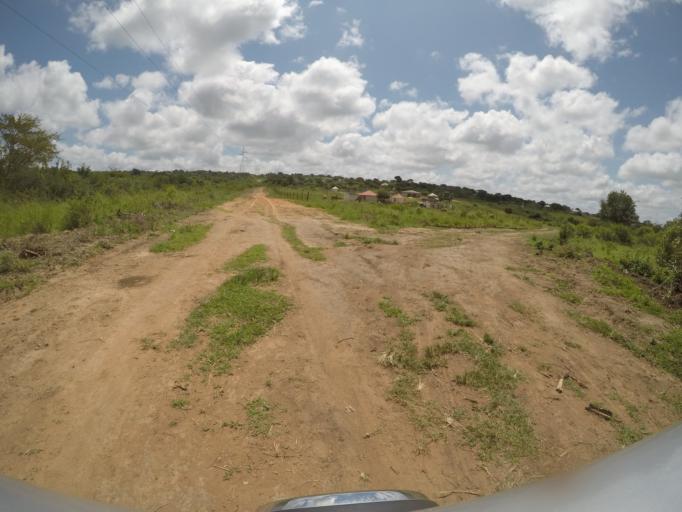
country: ZA
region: KwaZulu-Natal
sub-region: uThungulu District Municipality
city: Empangeni
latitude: -28.5903
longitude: 31.8390
